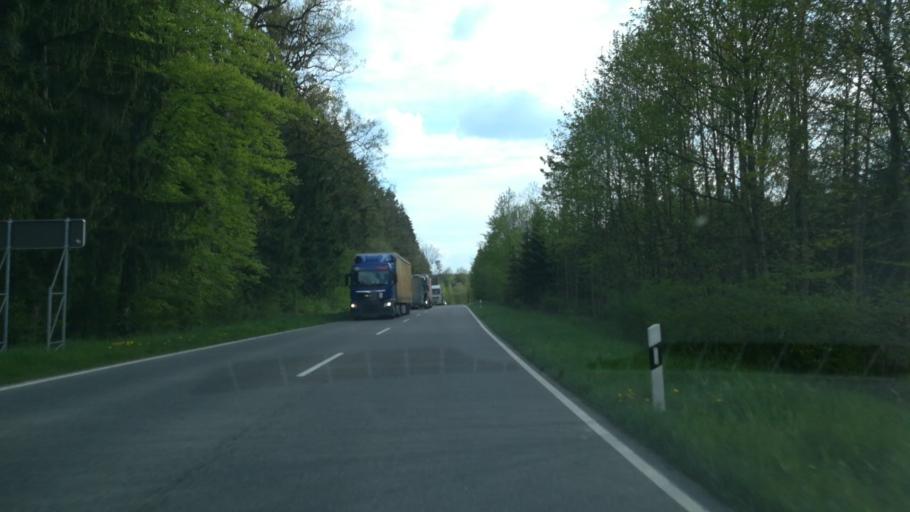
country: DE
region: Baden-Wuerttemberg
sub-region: Tuebingen Region
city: Messkirch
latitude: 47.9773
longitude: 9.0804
